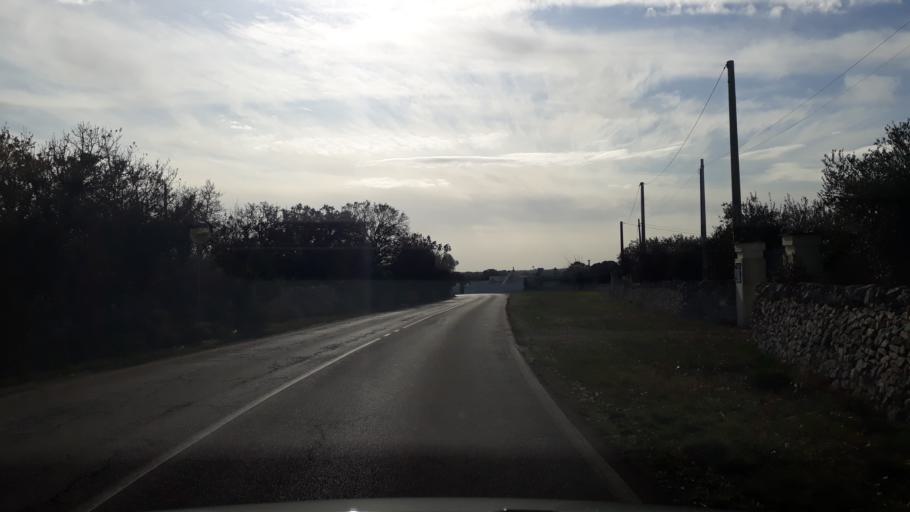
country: IT
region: Apulia
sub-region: Provincia di Taranto
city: Martina Franca
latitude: 40.6686
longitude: 17.3677
